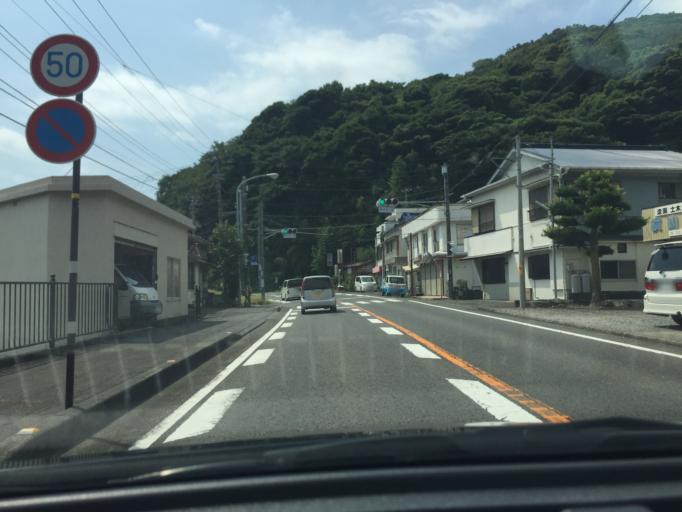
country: JP
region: Shizuoka
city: Ito
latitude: 34.8012
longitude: 139.0599
